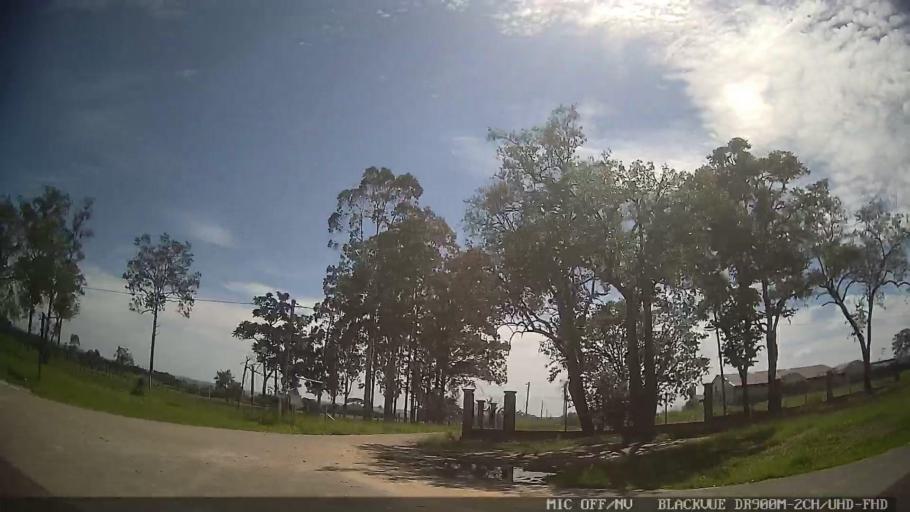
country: BR
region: Sao Paulo
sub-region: Boituva
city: Boituva
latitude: -23.1828
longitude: -47.6371
